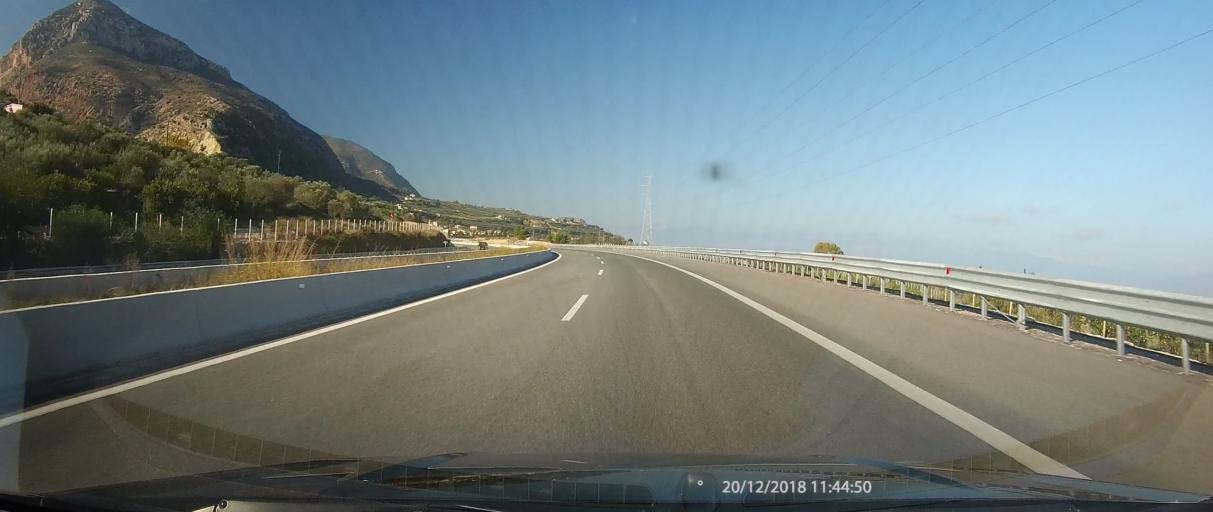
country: GR
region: Peloponnese
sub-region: Nomos Korinthias
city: Xylokastro
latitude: 38.0838
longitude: 22.5891
